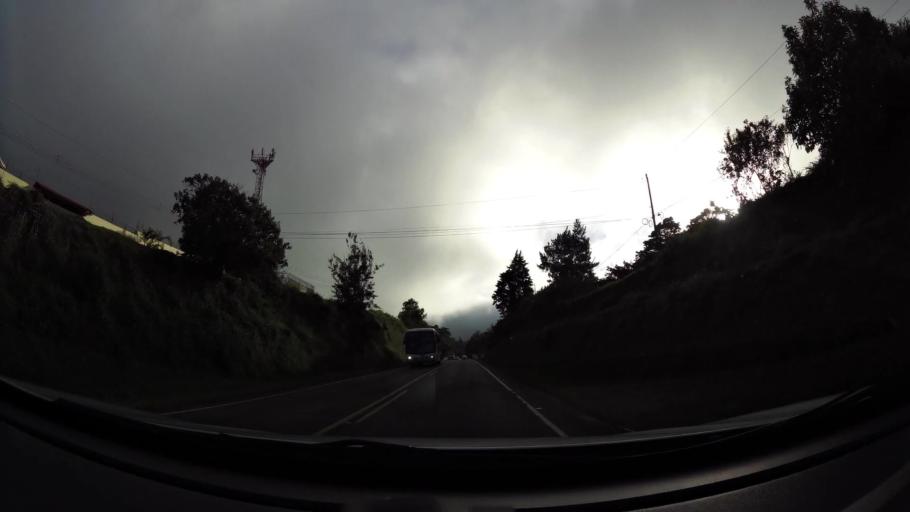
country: CR
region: Heredia
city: Angeles
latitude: 10.0296
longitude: -84.0154
